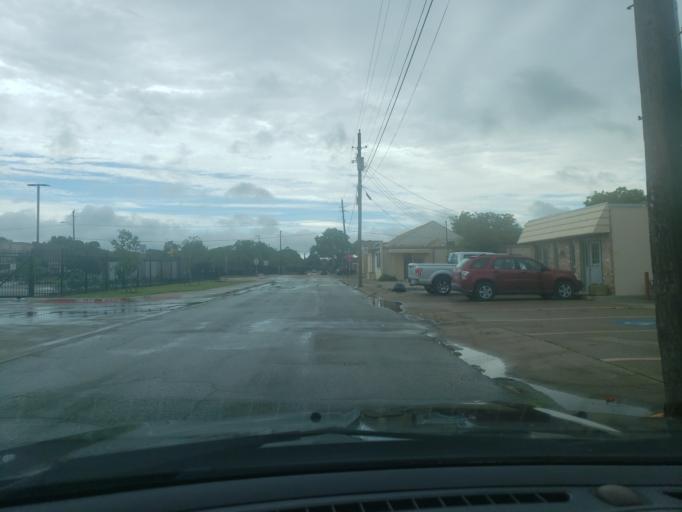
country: US
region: Texas
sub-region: Dallas County
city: Grand Prairie
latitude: 32.7463
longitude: -96.9998
